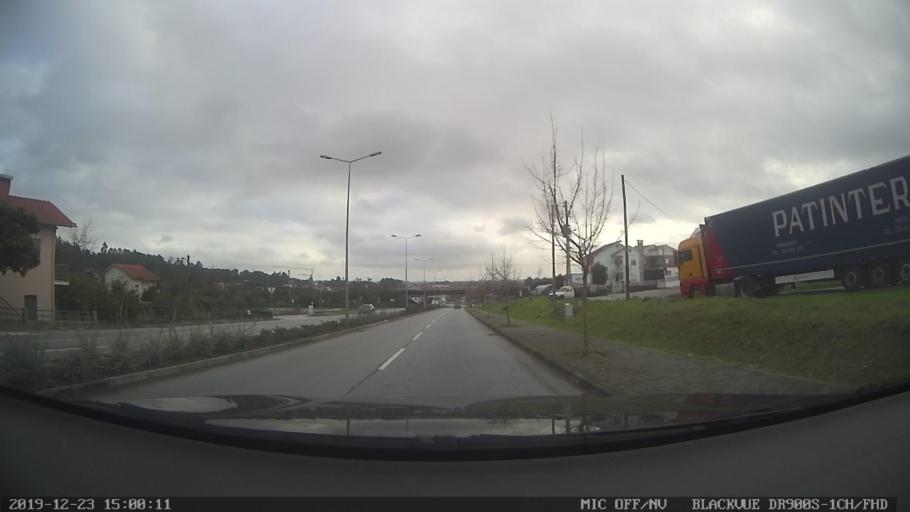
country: PT
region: Viseu
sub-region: Viseu
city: Abraveses
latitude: 40.6953
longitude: -7.9325
